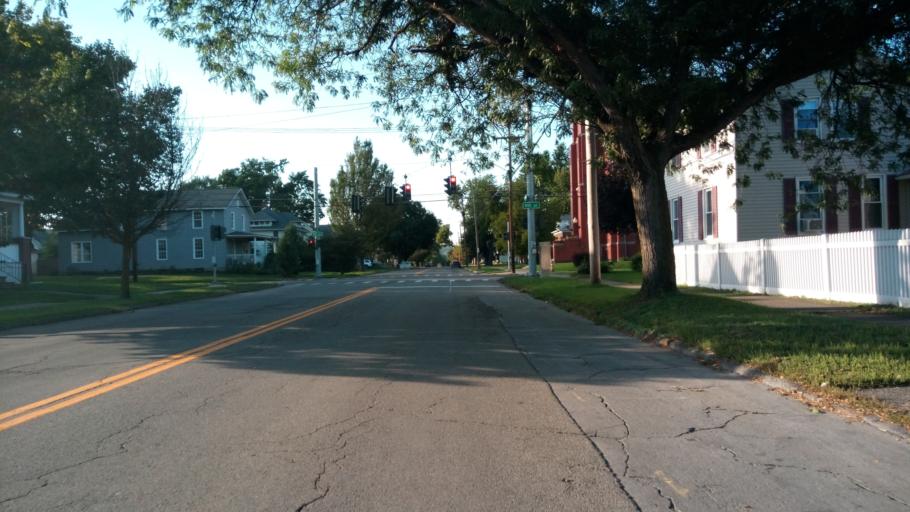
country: US
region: New York
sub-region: Chemung County
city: Elmira
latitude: 42.1003
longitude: -76.8207
